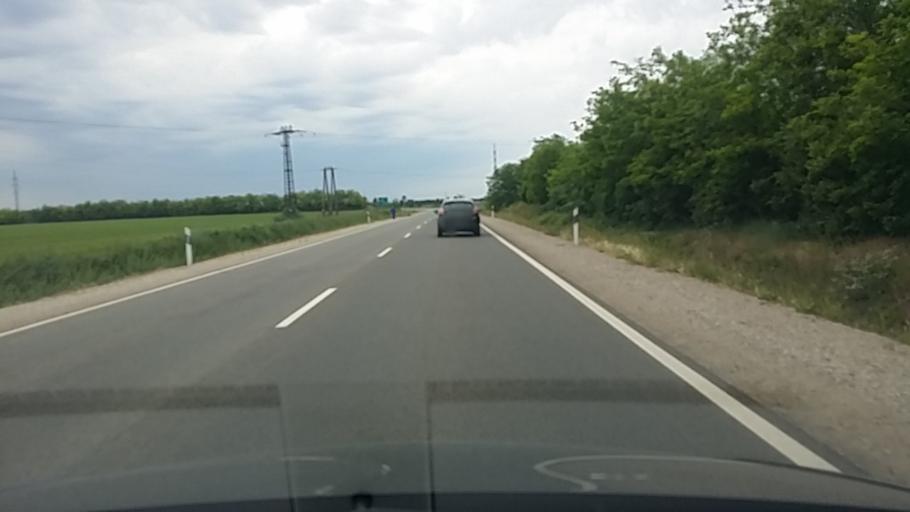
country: HU
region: Fejer
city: dunaujvaros
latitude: 46.9897
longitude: 18.8961
